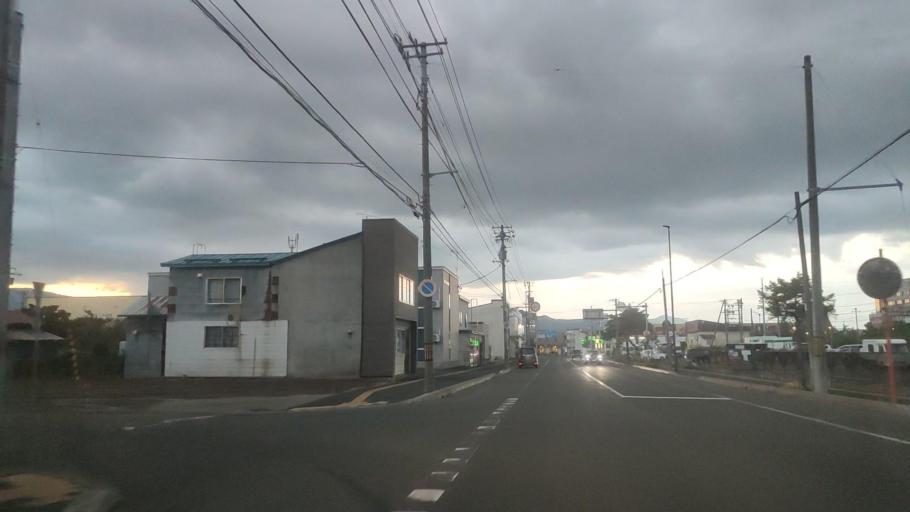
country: JP
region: Hokkaido
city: Shimo-furano
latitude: 43.3442
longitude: 142.3922
